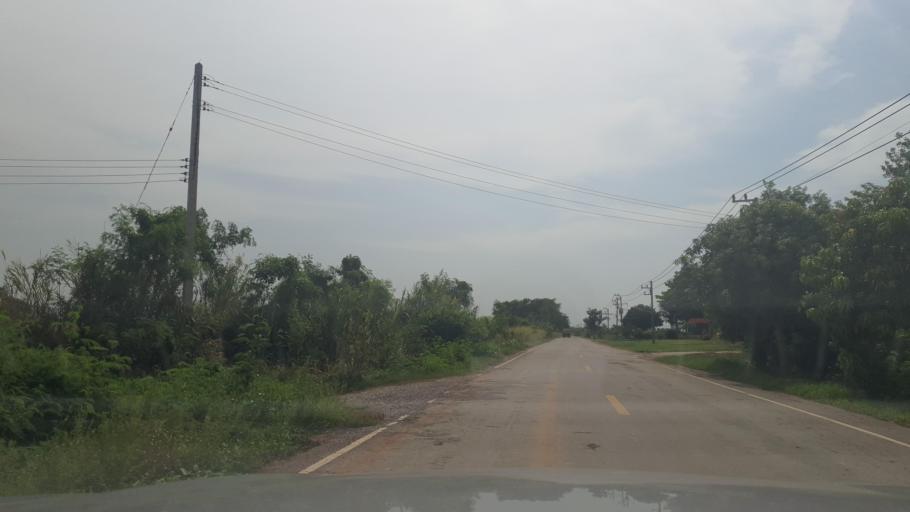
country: TH
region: Sukhothai
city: Si Samrong
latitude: 17.1166
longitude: 99.8793
